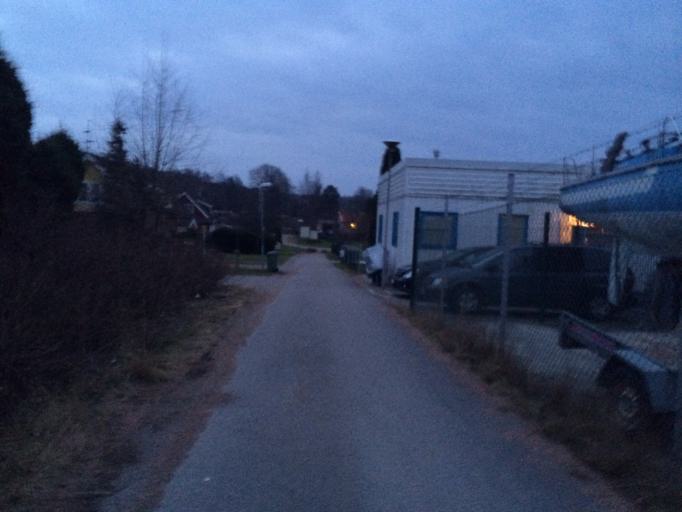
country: SE
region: Vaestra Goetaland
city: Svanesund
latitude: 58.1423
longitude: 11.8233
